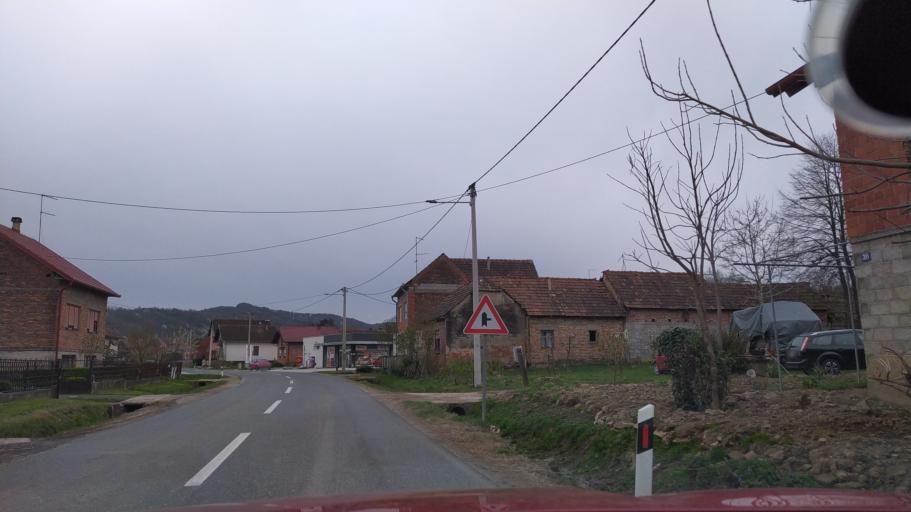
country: HR
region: Varazdinska
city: Ludbreg
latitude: 46.2356
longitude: 16.5474
